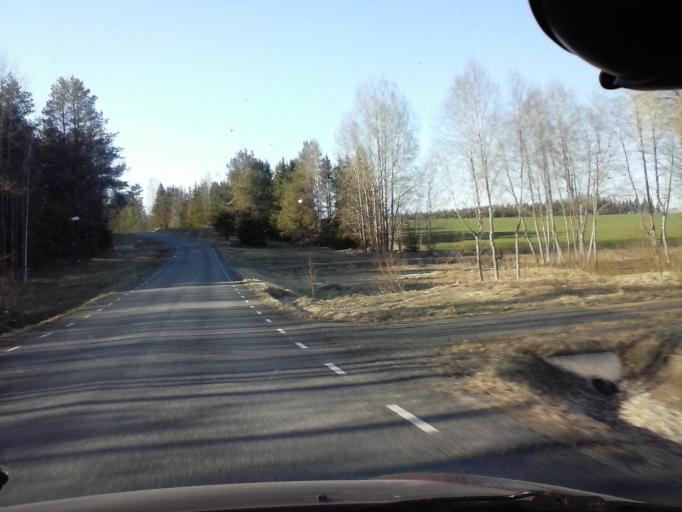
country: EE
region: Tartu
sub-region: UElenurme vald
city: Ulenurme
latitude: 58.1746
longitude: 26.8328
